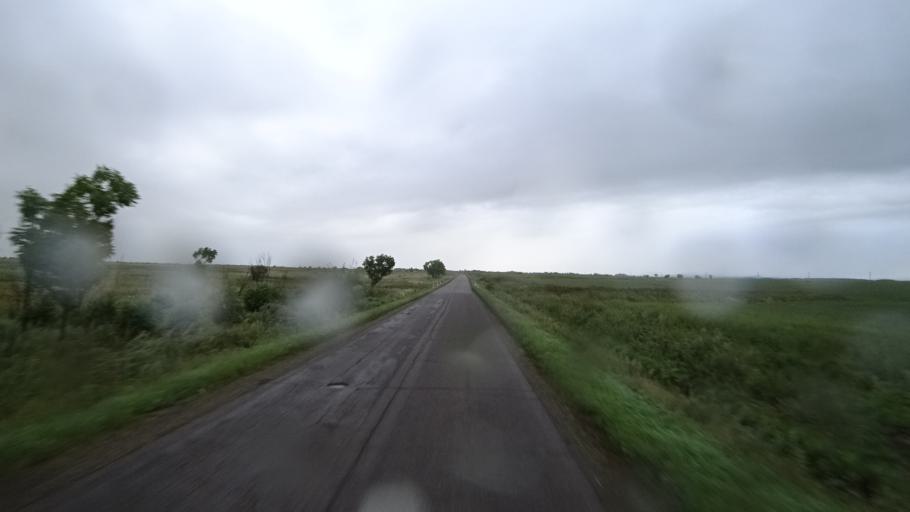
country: RU
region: Primorskiy
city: Chernigovka
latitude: 44.3853
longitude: 132.5295
